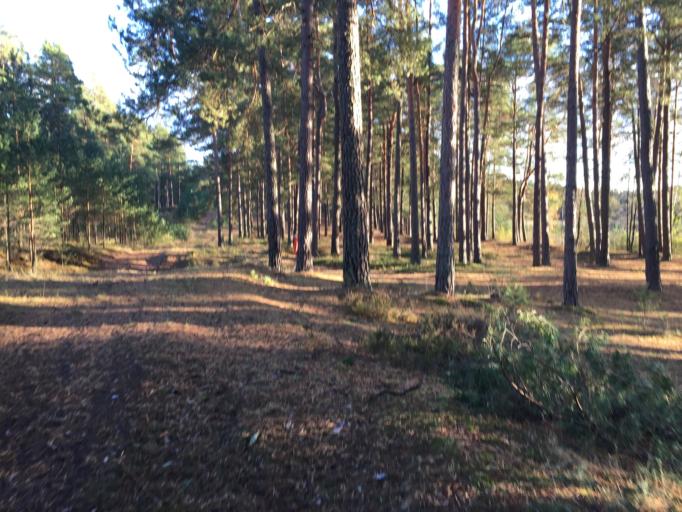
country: LV
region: Carnikava
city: Carnikava
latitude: 57.1706
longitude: 24.3335
